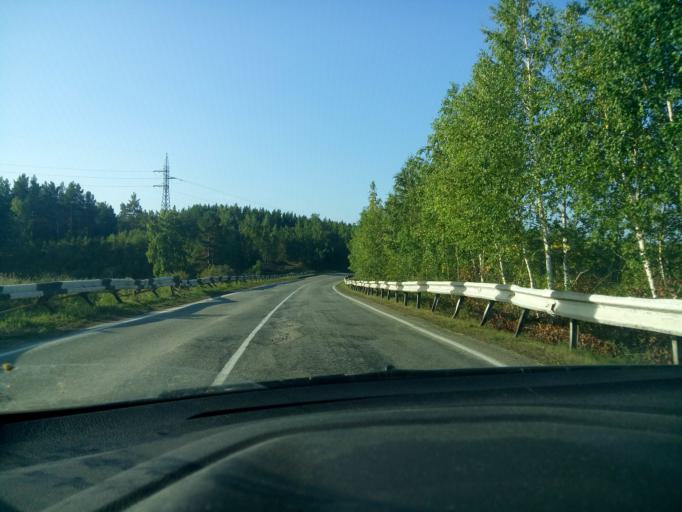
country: RU
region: Chelyabinsk
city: Kasli
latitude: 55.8687
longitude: 60.6985
